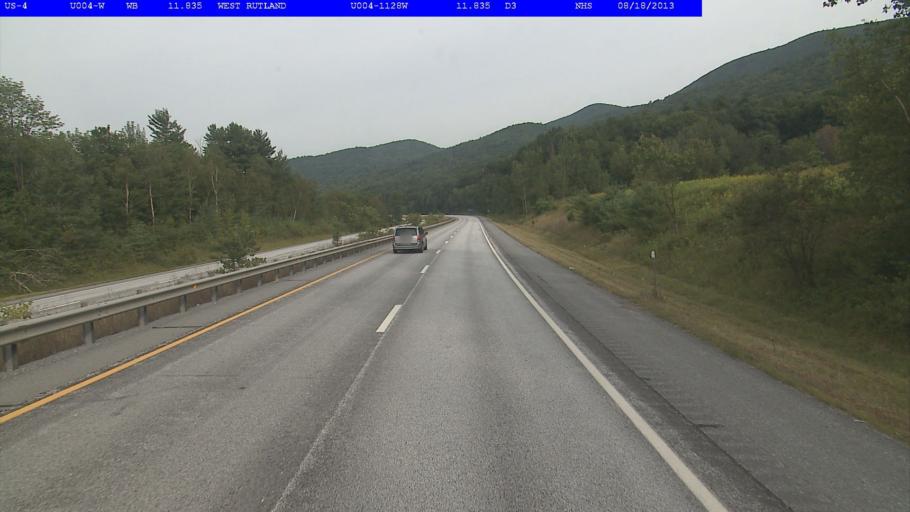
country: US
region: Vermont
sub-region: Rutland County
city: West Rutland
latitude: 43.6098
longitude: -73.0872
